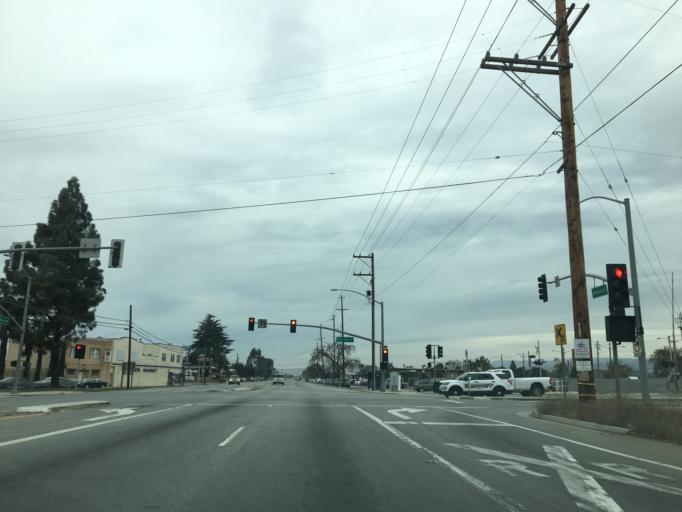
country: US
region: California
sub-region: Santa Clara County
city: San Martin
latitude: 37.0845
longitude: -121.6100
